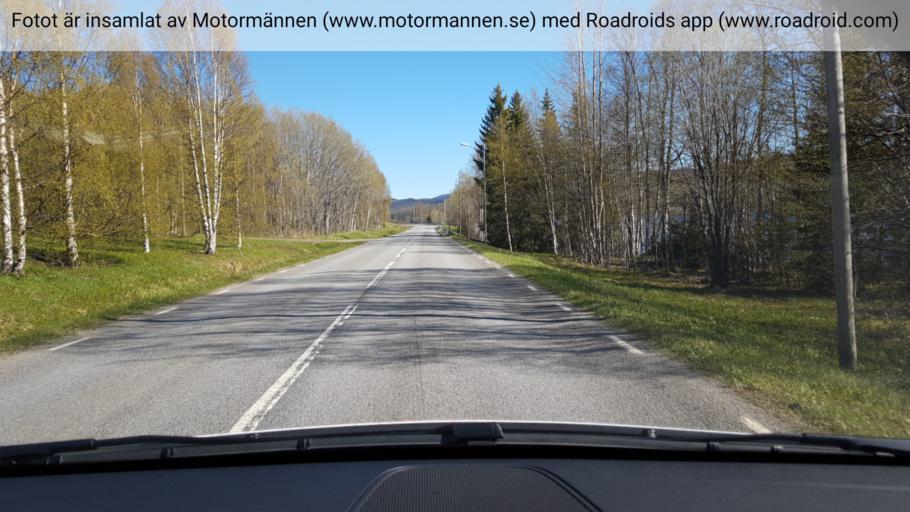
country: NO
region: Nord-Trondelag
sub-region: Lierne
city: Sandvika
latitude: 64.3871
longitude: 14.5300
